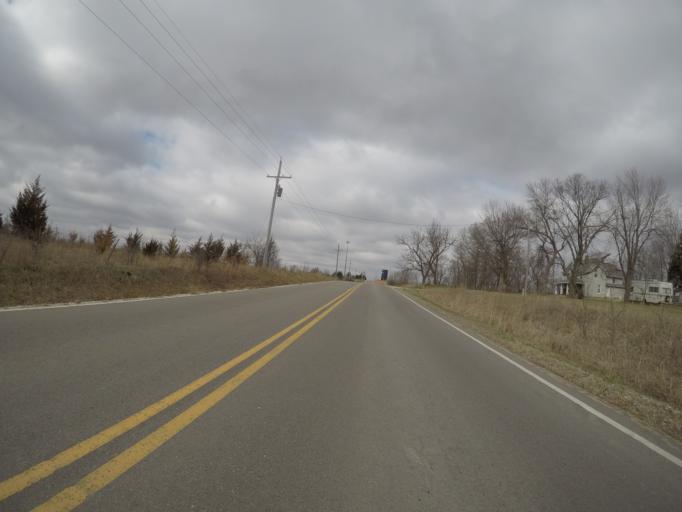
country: US
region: Kansas
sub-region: Pottawatomie County
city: Westmoreland
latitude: 39.3993
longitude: -96.4215
